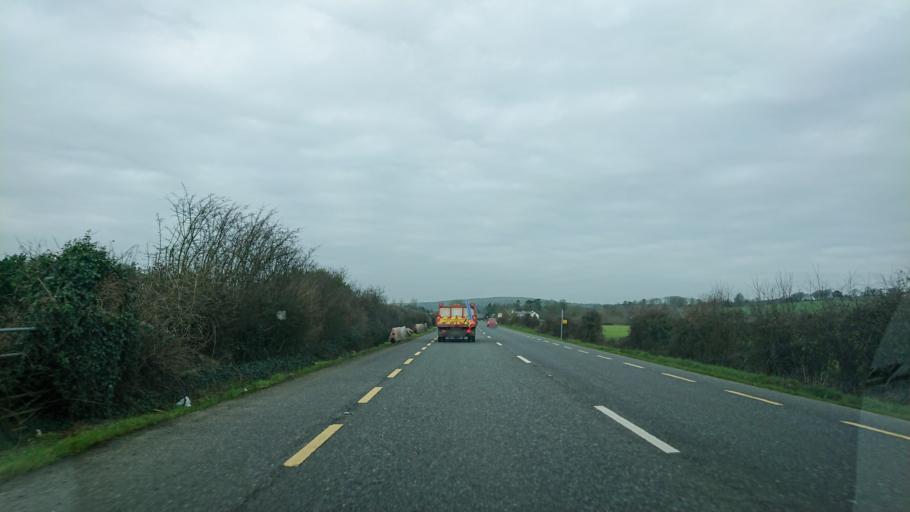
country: IE
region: Munster
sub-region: County Cork
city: Castlemartyr
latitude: 51.9406
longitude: -7.9824
